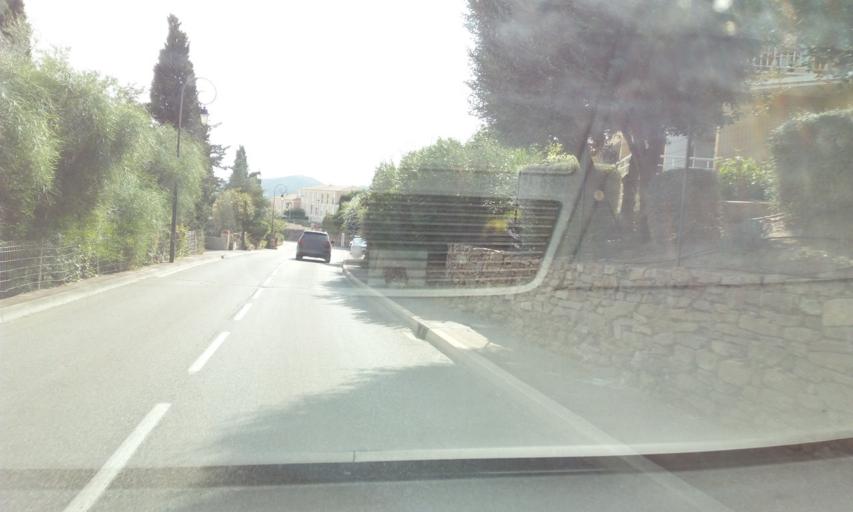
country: FR
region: Provence-Alpes-Cote d'Azur
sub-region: Departement du Var
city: Bormes-les-Mimosas
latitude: 43.1465
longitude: 6.3400
